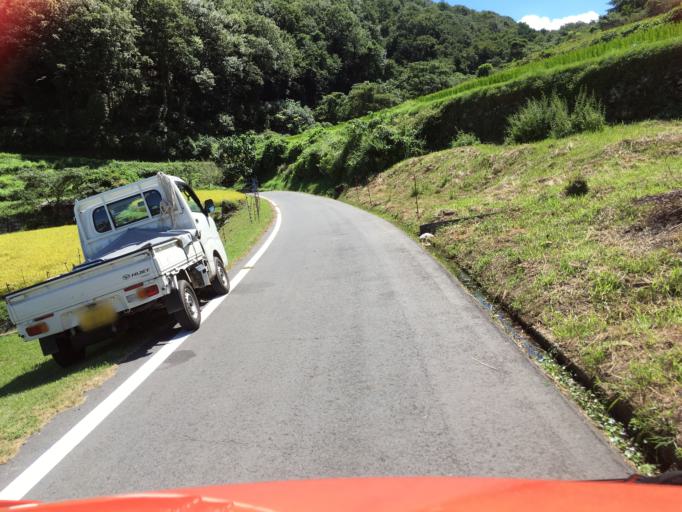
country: JP
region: Okayama
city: Tsuyama
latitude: 34.8965
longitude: 134.1372
